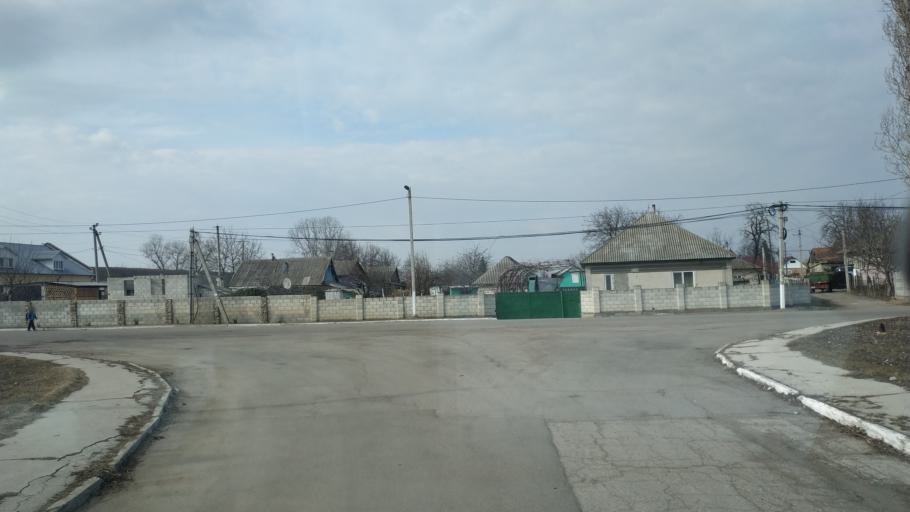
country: MD
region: Anenii Noi
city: Anenii Noi
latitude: 46.9023
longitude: 29.1350
